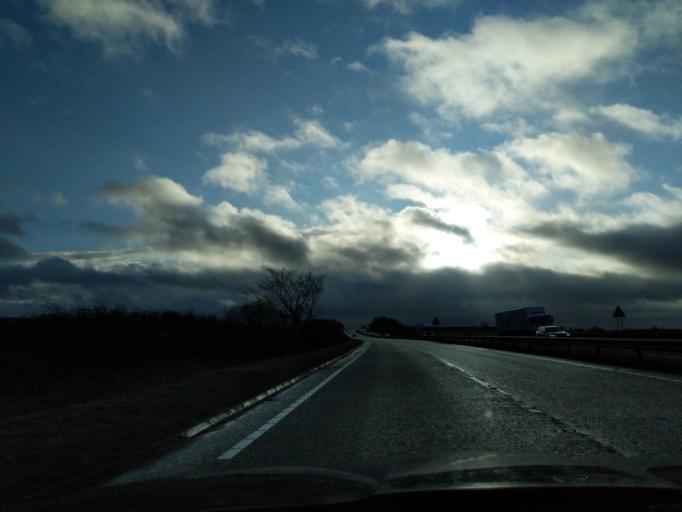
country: GB
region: England
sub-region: Northumberland
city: Alnwick
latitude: 55.3716
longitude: -1.7240
